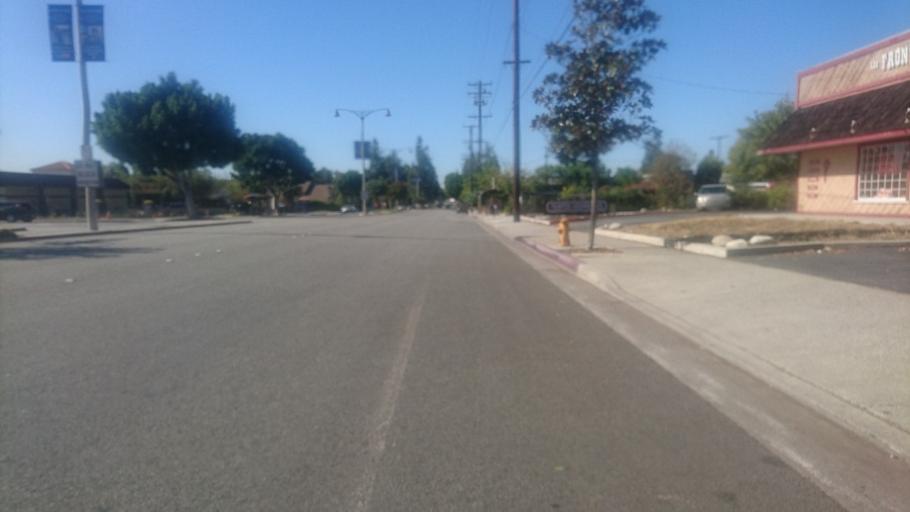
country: US
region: California
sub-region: Los Angeles County
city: Bradbury
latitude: 34.1398
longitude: -117.9587
